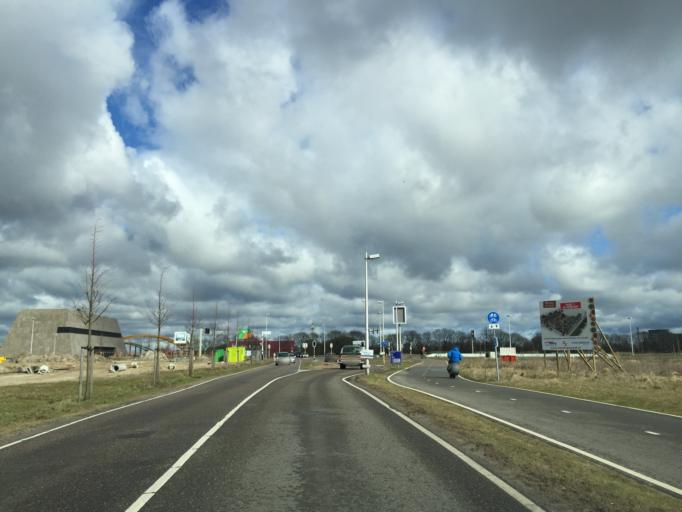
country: NL
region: Utrecht
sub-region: Stichtse Vecht
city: Maarssen
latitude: 52.0935
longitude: 5.0685
